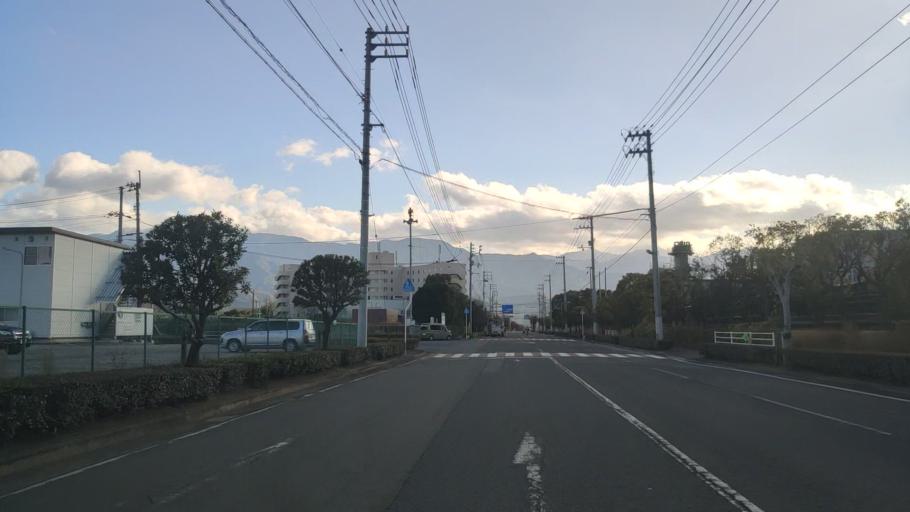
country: JP
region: Ehime
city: Saijo
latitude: 33.9375
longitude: 133.1920
